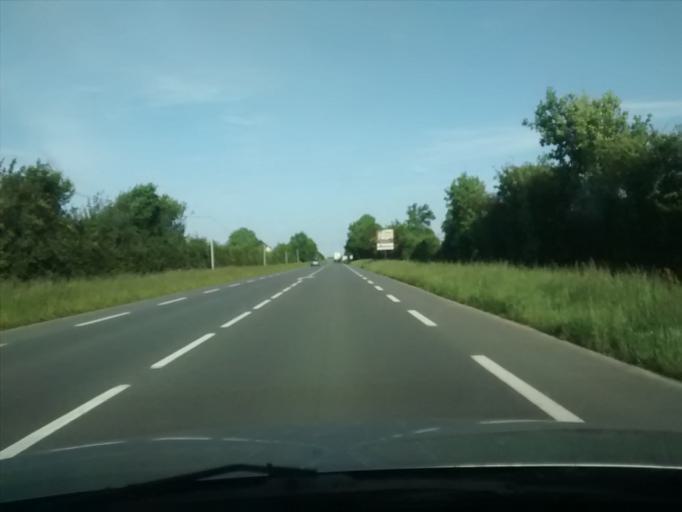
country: FR
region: Pays de la Loire
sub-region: Departement de la Mayenne
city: Vaiges
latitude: 48.0447
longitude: -0.4966
